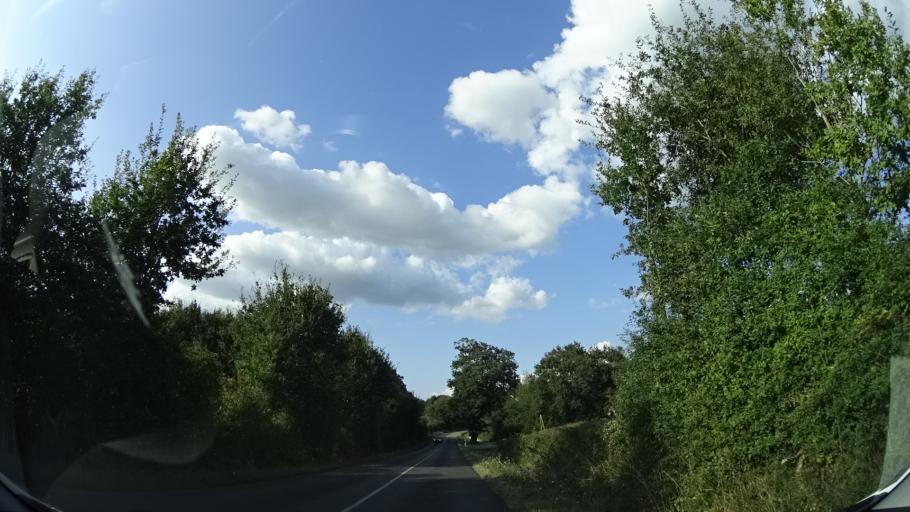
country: FR
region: Pays de la Loire
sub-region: Departement de la Loire-Atlantique
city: Suce-sur-Erdre
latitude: 47.3634
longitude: -1.5267
